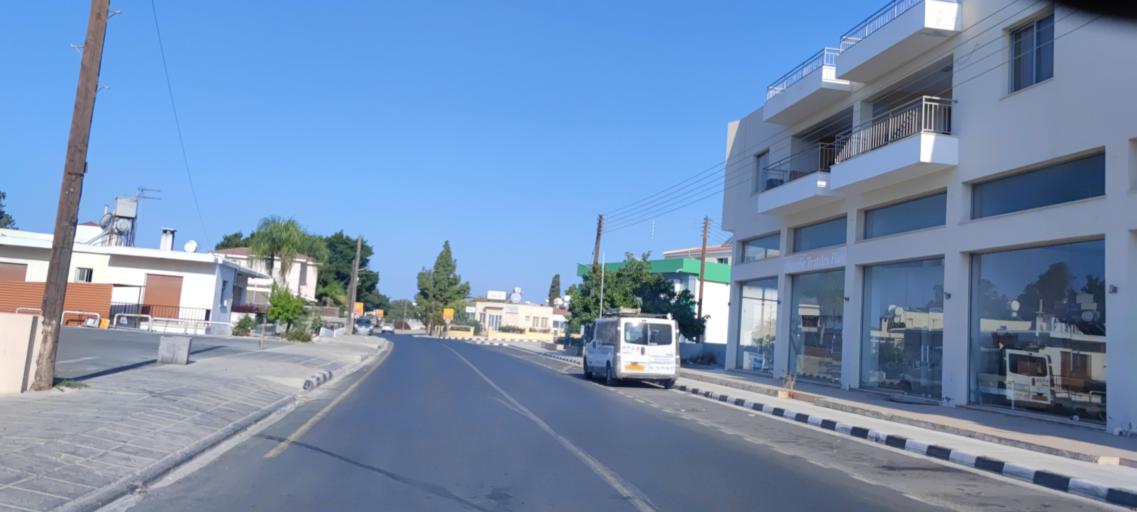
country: CY
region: Pafos
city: Chlorakas
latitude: 34.7934
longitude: 32.4144
